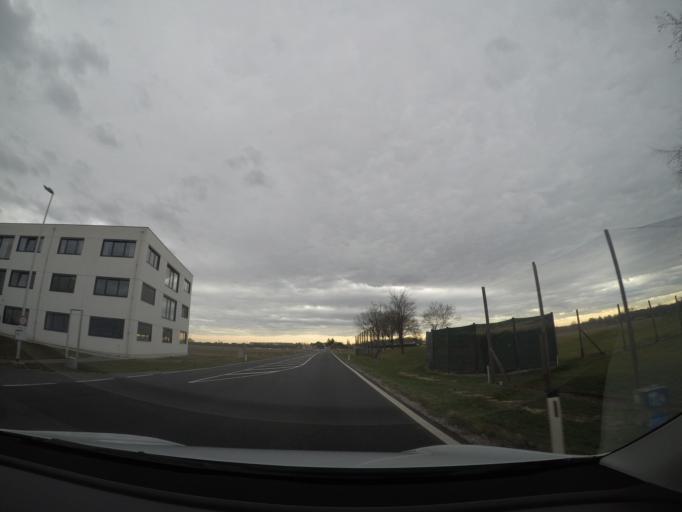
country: AT
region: Lower Austria
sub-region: Politischer Bezirk Modling
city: Achau
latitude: 48.0813
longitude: 16.3701
